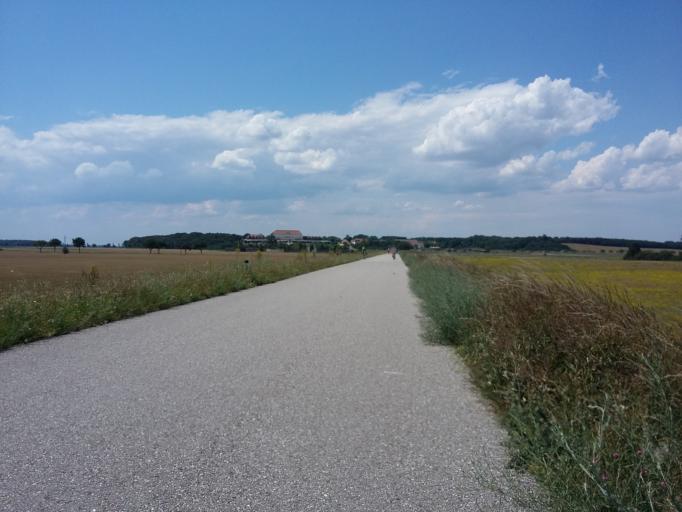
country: AT
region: Lower Austria
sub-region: Politischer Bezirk Bruck an der Leitha
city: Hainburg an der Donau
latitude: 48.2126
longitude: 16.9544
